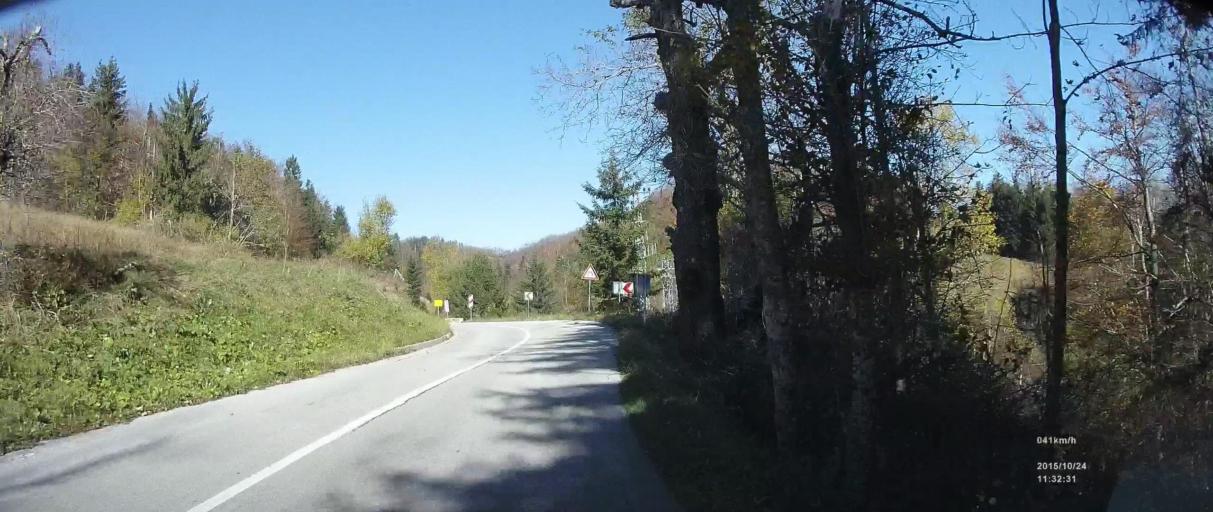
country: HR
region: Primorsko-Goranska
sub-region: Grad Delnice
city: Delnice
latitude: 45.3897
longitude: 14.6872
